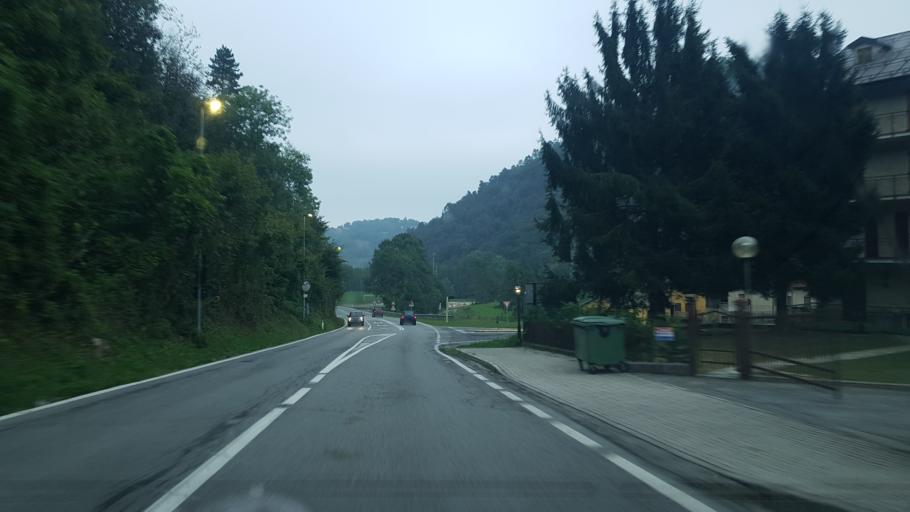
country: IT
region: Piedmont
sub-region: Provincia di Cuneo
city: Frabosa Sottana
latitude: 44.3063
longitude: 7.8012
